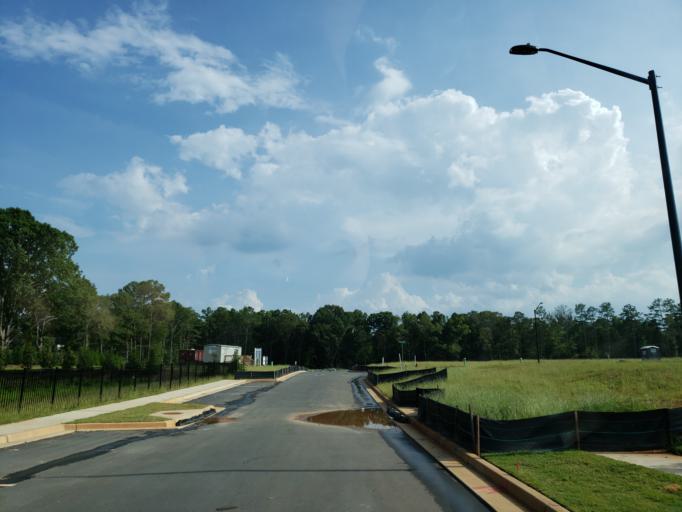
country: US
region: Georgia
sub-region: Cobb County
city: Kennesaw
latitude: 34.0830
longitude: -84.5847
